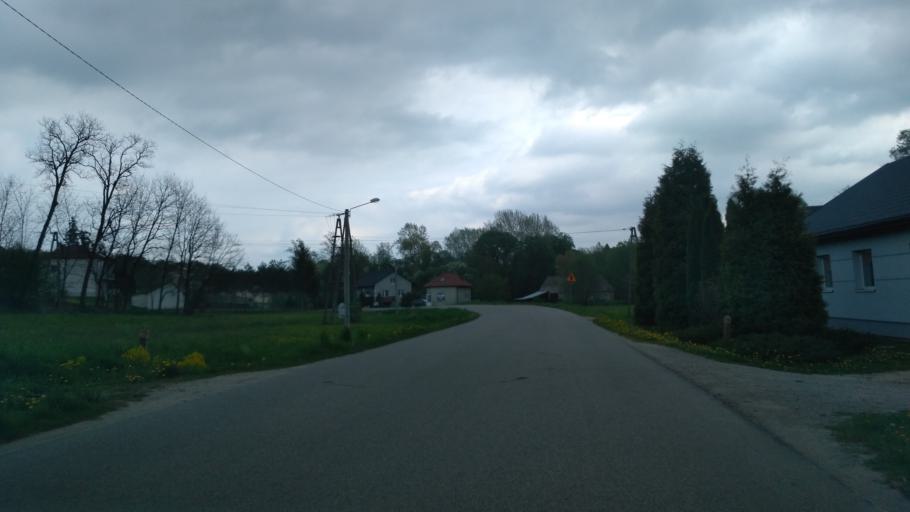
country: PL
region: Subcarpathian Voivodeship
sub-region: Powiat debicki
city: Leki Gorne
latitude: 49.9734
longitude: 21.1777
